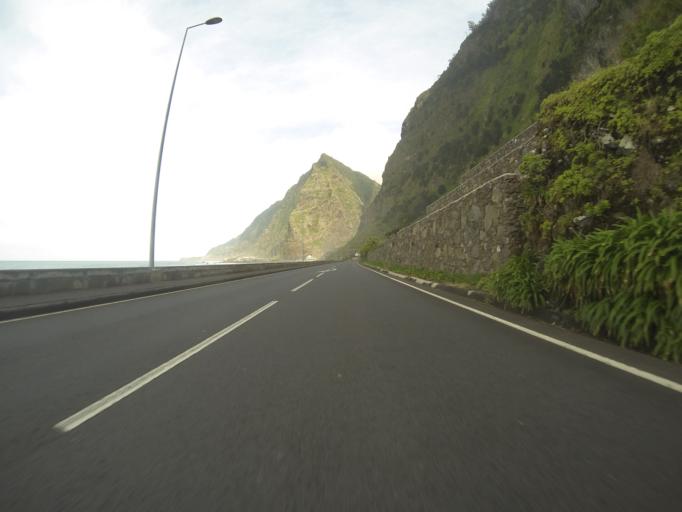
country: PT
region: Madeira
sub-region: Sao Vicente
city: Sao Vicente
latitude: 32.8095
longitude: -17.0610
